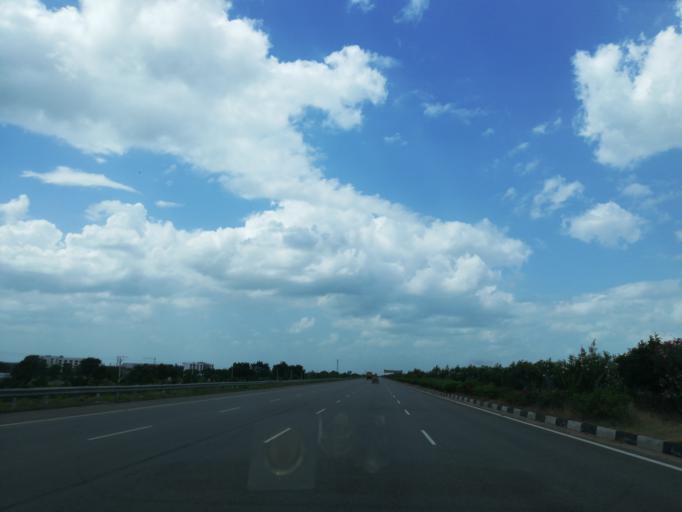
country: IN
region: Telangana
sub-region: Medak
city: Serilingampalle
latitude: 17.4777
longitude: 78.2472
